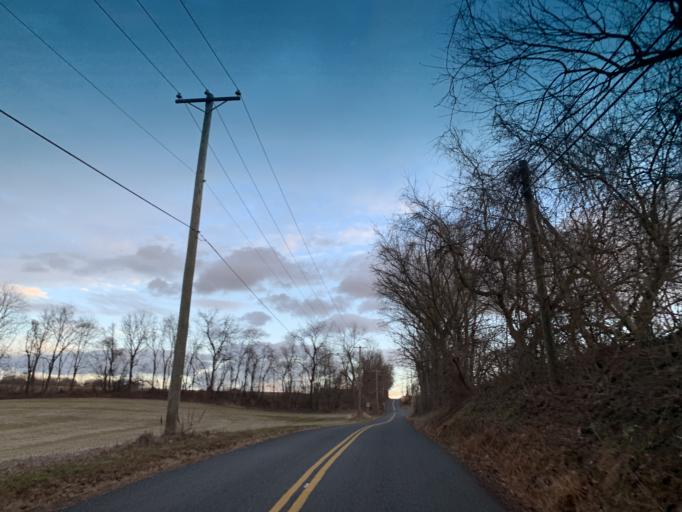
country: US
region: Pennsylvania
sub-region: York County
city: Susquehanna Trails
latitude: 39.6622
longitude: -76.3181
